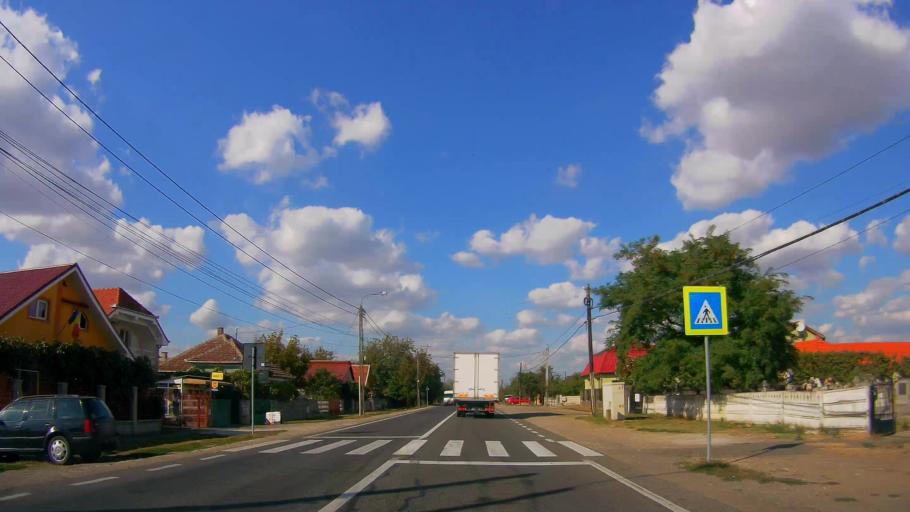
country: RO
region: Satu Mare
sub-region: Oras Ardud
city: Madaras
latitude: 47.7375
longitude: 22.8826
